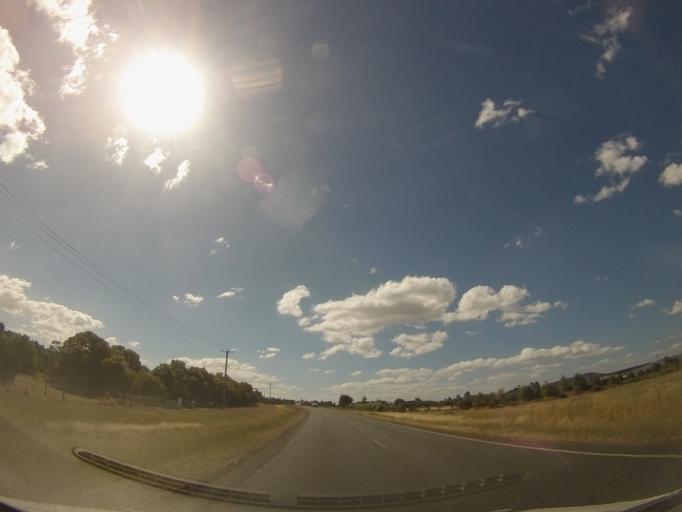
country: AU
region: Tasmania
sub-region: Clarence
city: Seven Mile Beach
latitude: -42.8489
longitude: 147.4831
